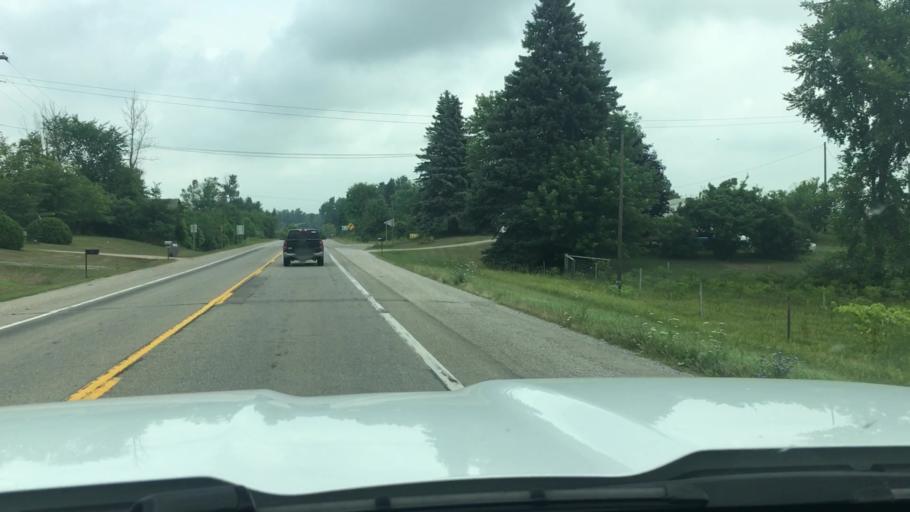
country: US
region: Michigan
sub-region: Lapeer County
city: Imlay City
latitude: 43.0792
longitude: -83.0756
